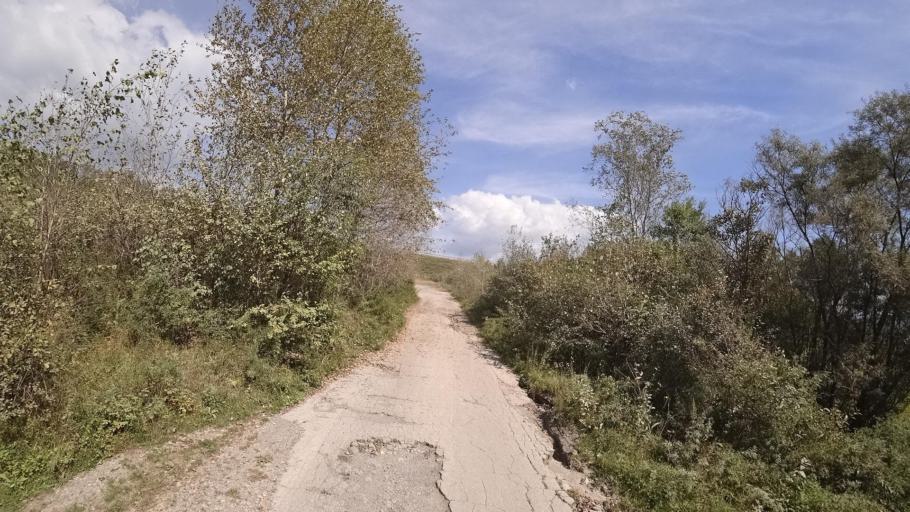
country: RU
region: Jewish Autonomous Oblast
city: Londoko
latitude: 49.0070
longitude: 131.9142
